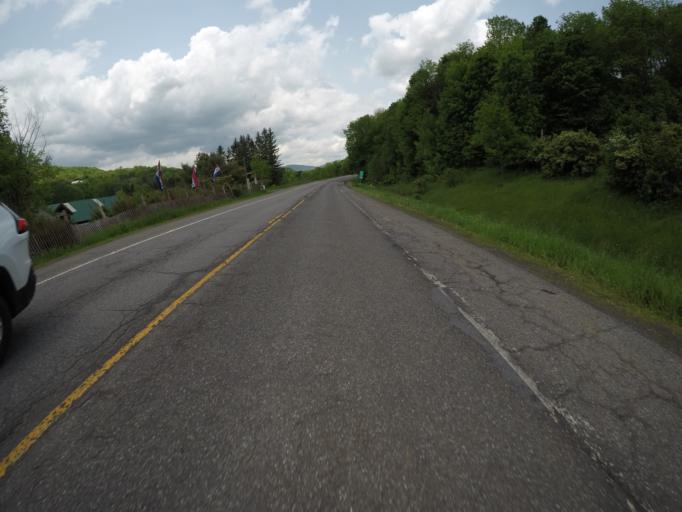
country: US
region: New York
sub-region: Delaware County
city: Stamford
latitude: 42.2429
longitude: -74.5993
